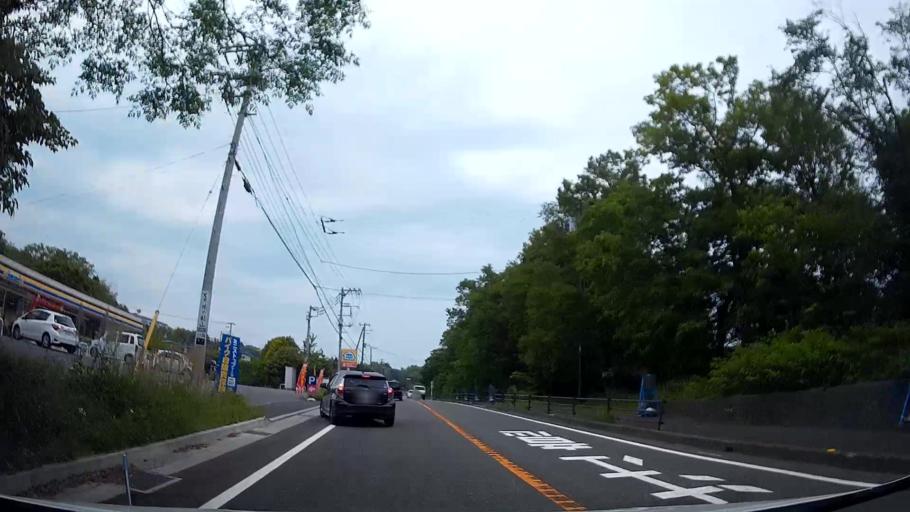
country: JP
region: Shizuoka
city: Ito
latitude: 34.8956
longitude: 139.1195
